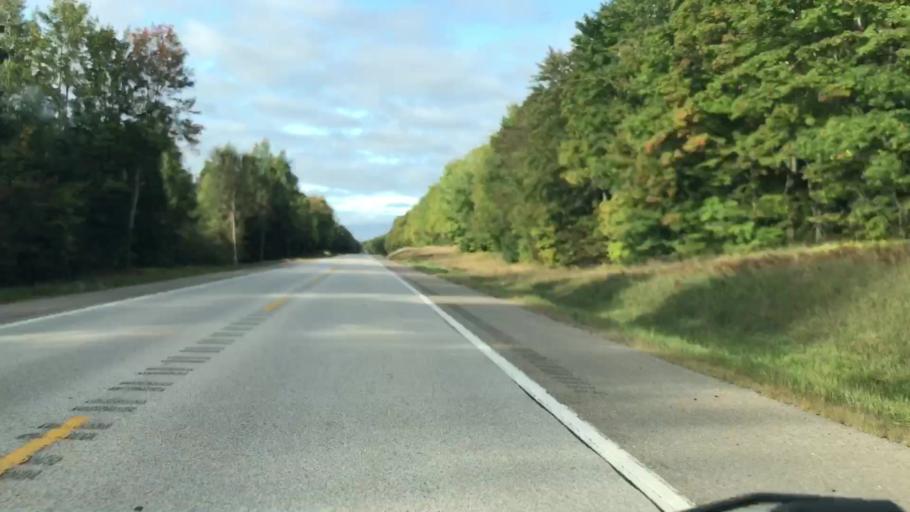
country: US
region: Michigan
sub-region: Luce County
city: Newberry
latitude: 46.3414
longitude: -85.0386
